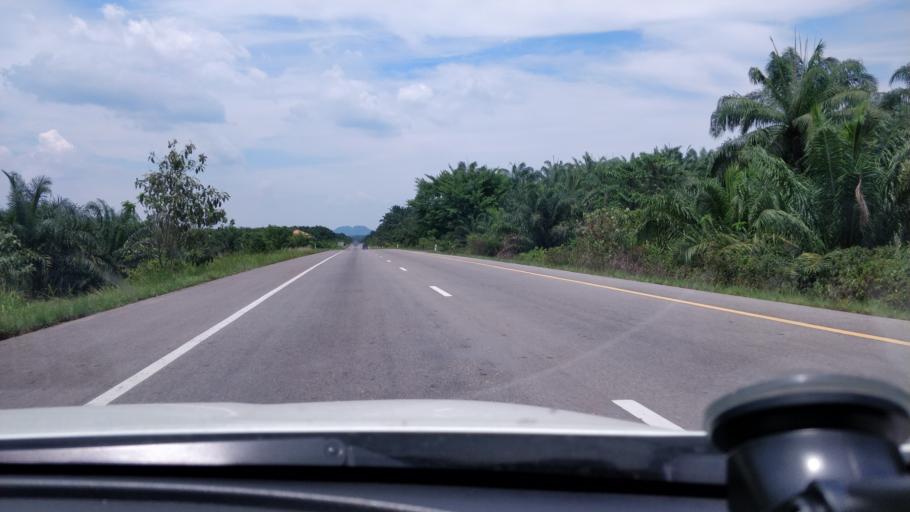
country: TH
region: Krabi
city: Plai Phraya
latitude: 8.5213
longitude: 98.8949
